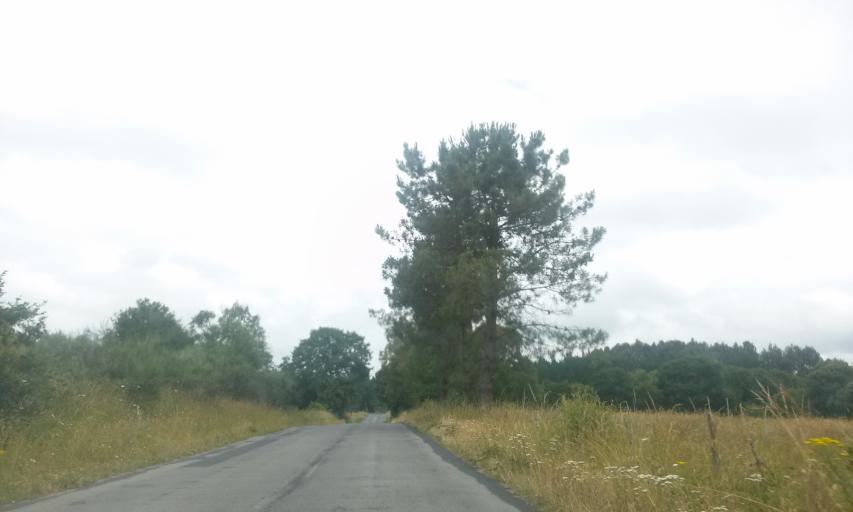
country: ES
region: Galicia
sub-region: Provincia de Lugo
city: Friol
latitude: 43.0960
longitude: -7.8087
